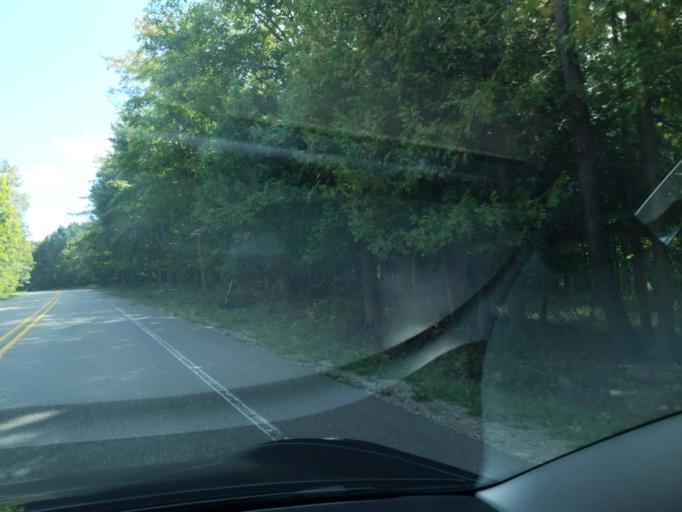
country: US
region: Michigan
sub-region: Antrim County
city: Bellaire
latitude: 45.0556
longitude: -85.3186
